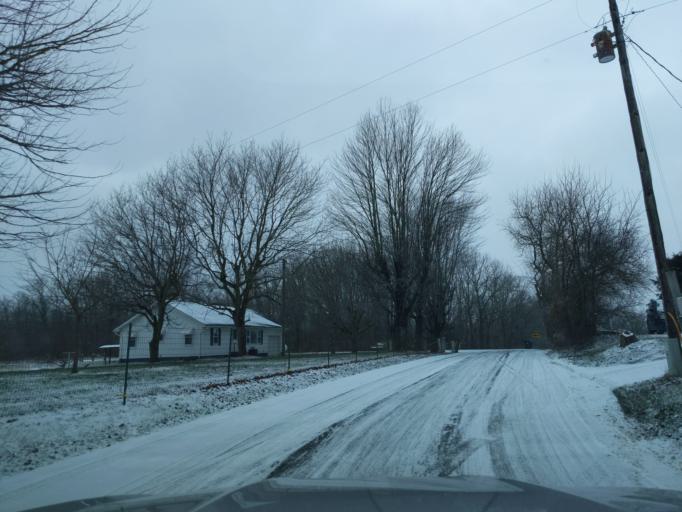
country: US
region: Indiana
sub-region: Decatur County
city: Westport
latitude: 39.2195
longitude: -85.5176
